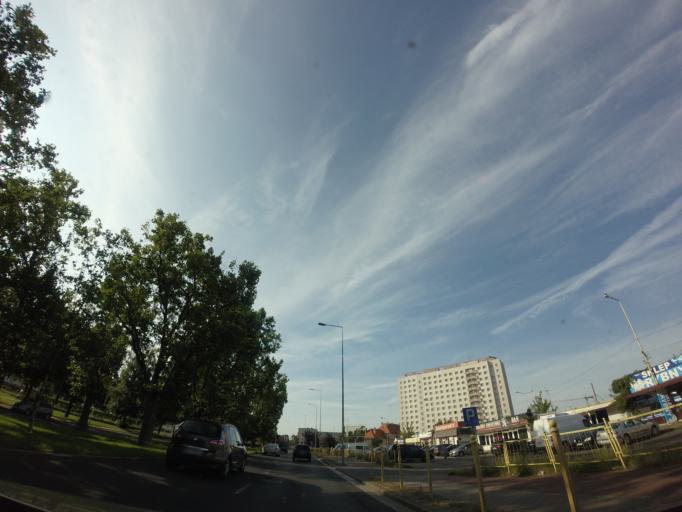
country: PL
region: West Pomeranian Voivodeship
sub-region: Szczecin
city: Szczecin
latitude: 53.4247
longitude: 14.5314
